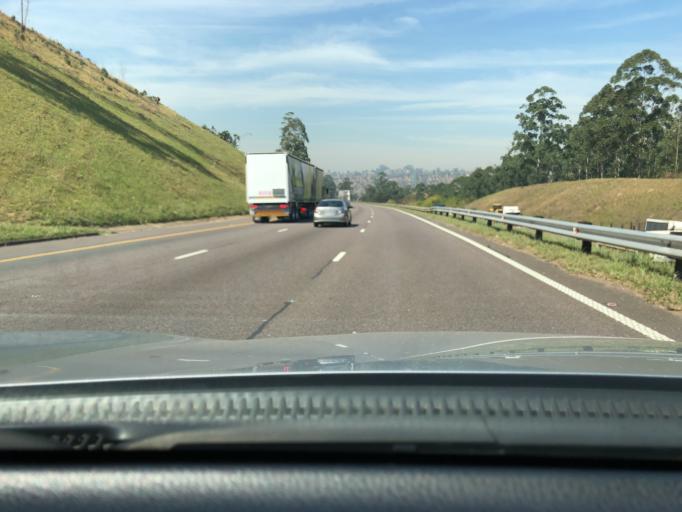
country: ZA
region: KwaZulu-Natal
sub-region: eThekwini Metropolitan Municipality
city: Mpumalanga
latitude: -29.8181
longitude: 30.7751
